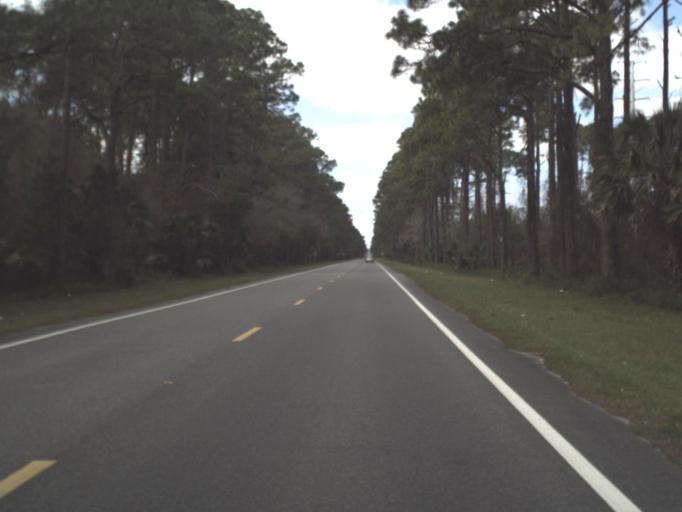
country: US
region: Florida
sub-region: Franklin County
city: Apalachicola
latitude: 29.7151
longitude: -85.0290
